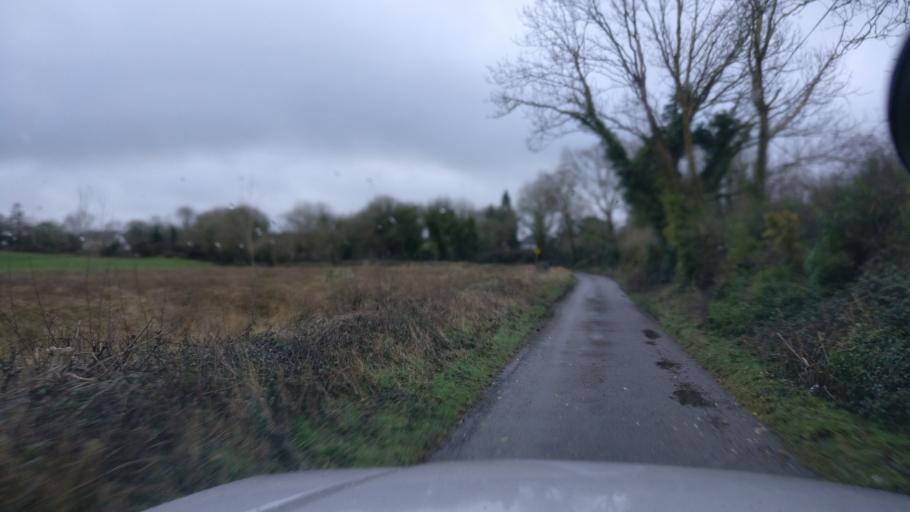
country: IE
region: Connaught
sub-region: County Galway
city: Athenry
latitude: 53.2118
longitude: -8.6979
